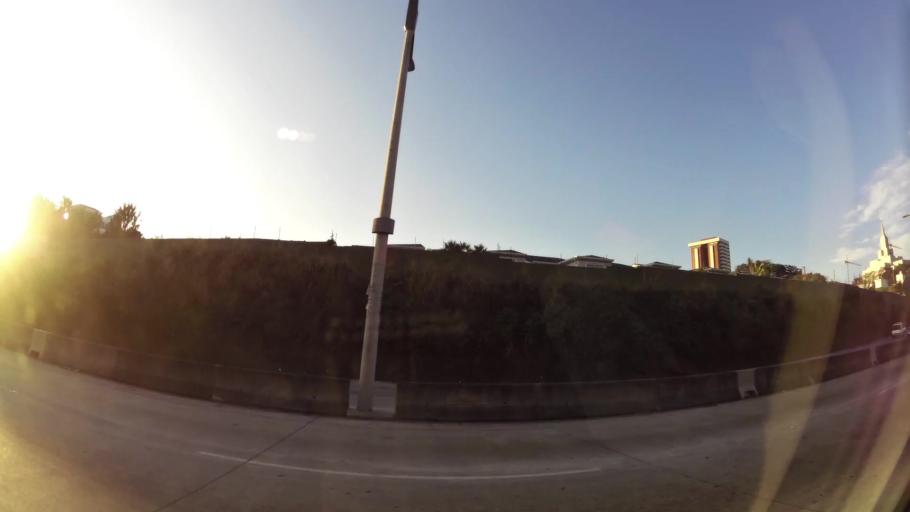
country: SV
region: La Libertad
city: Antiguo Cuscatlan
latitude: 13.6846
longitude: -89.2448
